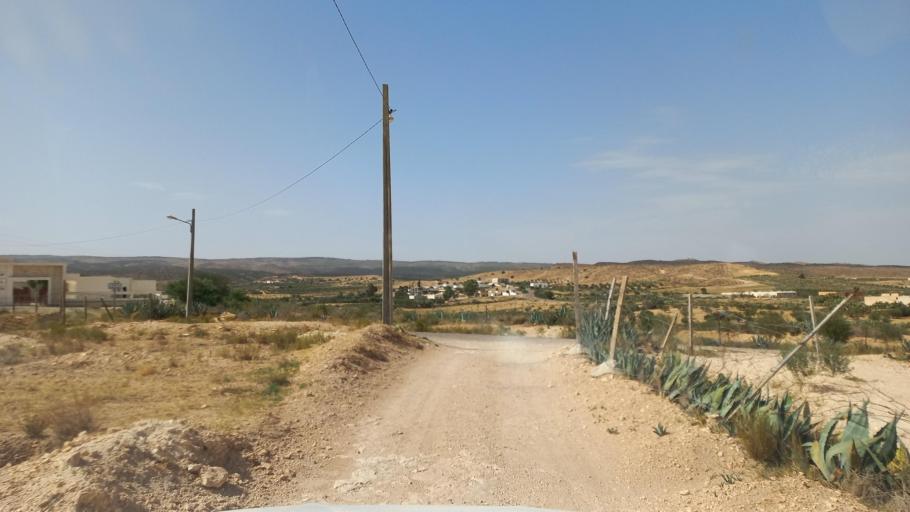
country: TN
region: Al Qasrayn
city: Kasserine
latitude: 35.2982
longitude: 8.9520
